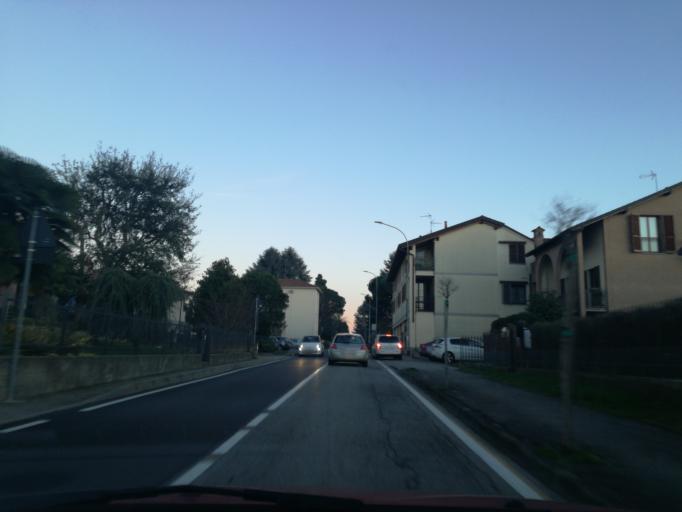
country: IT
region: Lombardy
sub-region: Provincia di Lecco
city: Osnago
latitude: 45.6688
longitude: 9.3936
